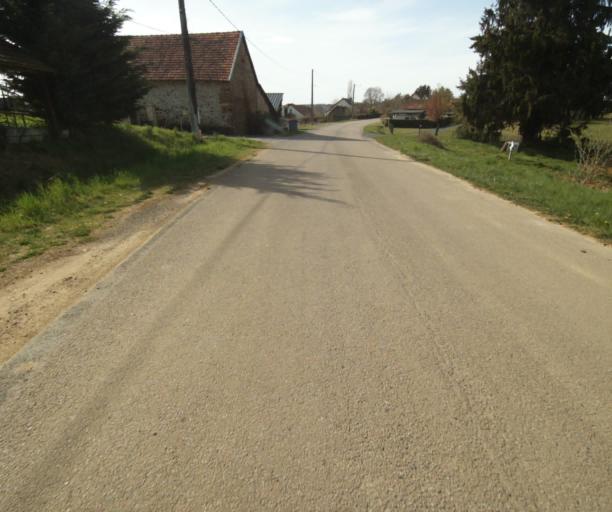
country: FR
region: Limousin
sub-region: Departement de la Correze
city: Naves
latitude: 45.3348
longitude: 1.7516
